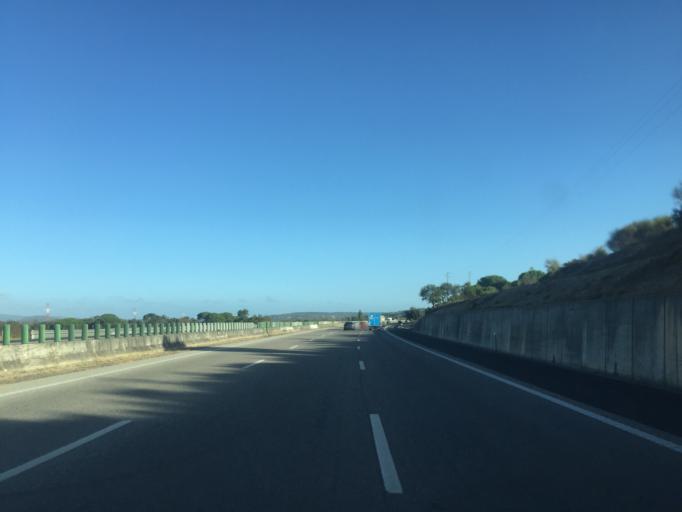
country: PT
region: Lisbon
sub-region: Alenquer
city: Carregado
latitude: 39.0582
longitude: -8.9415
